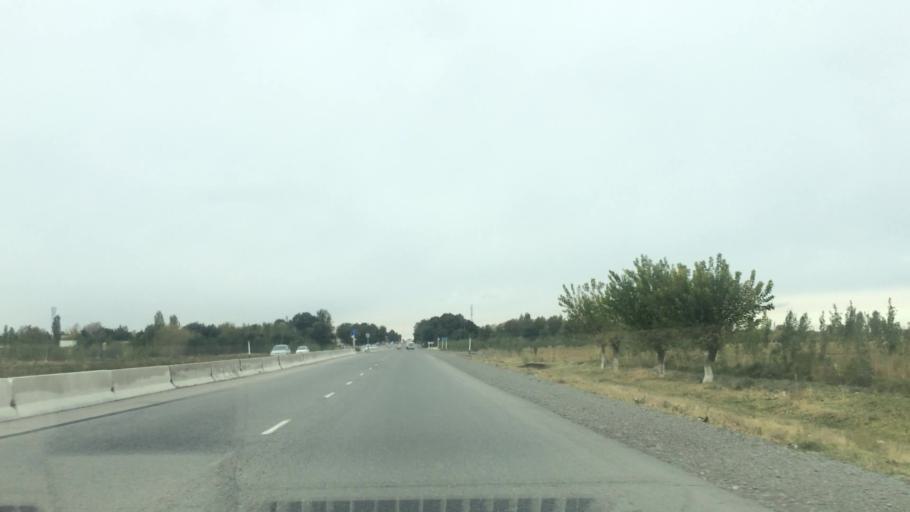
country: UZ
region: Samarqand
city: Bulung'ur
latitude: 39.7407
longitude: 67.1899
